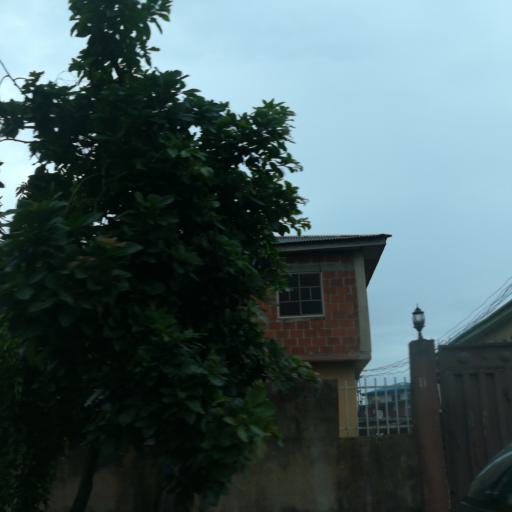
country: NG
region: Lagos
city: Oshodi
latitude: 6.5528
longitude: 3.3418
